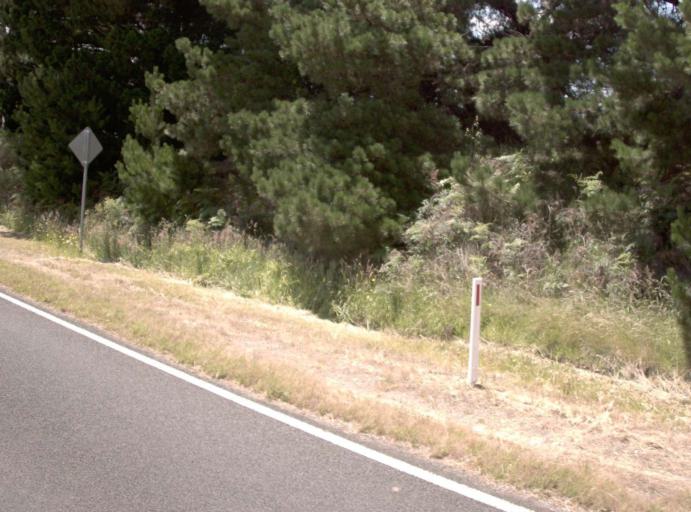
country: AU
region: Victoria
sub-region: Baw Baw
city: Warragul
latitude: -38.5150
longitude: 146.0544
